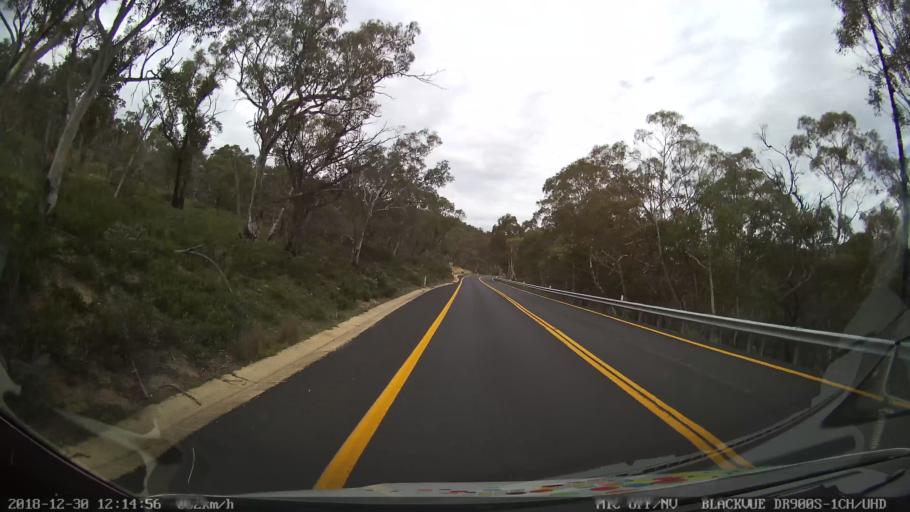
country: AU
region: New South Wales
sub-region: Snowy River
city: Jindabyne
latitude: -36.3431
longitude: 148.5760
